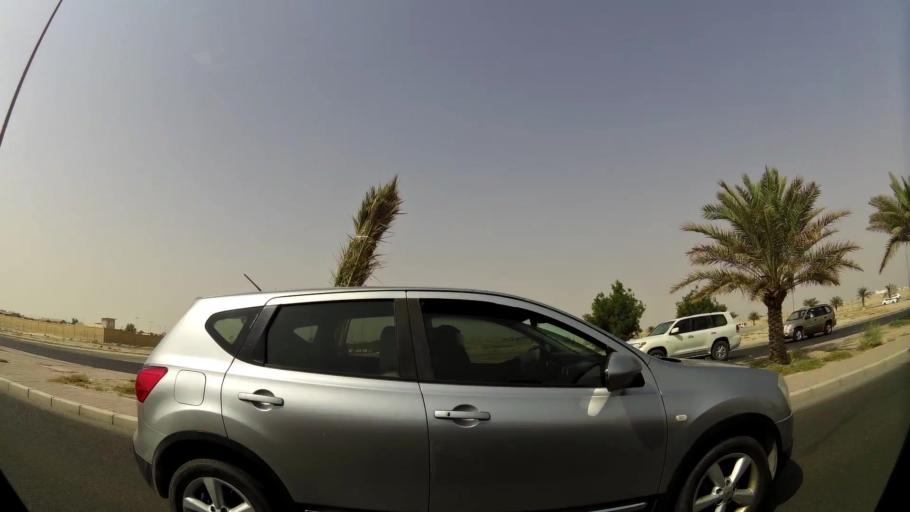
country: KW
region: Muhafazat al Jahra'
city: Al Jahra'
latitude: 29.3191
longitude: 47.7124
